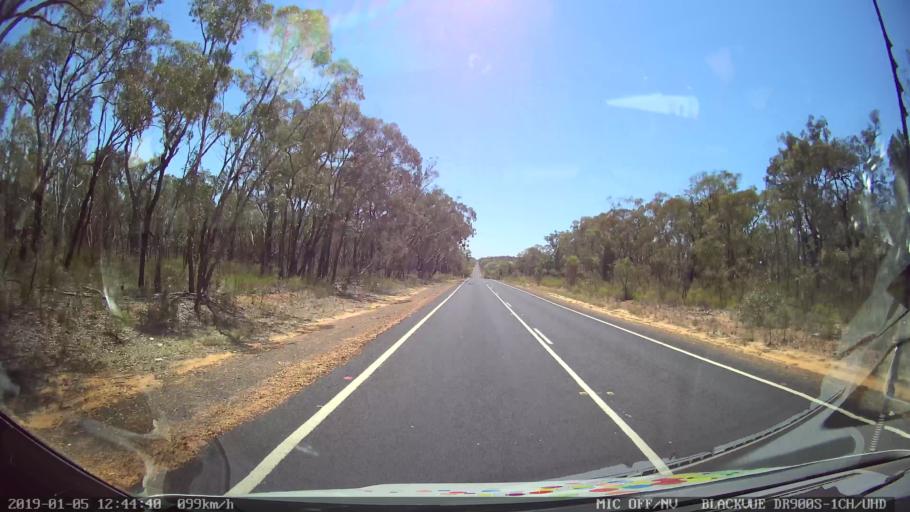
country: AU
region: New South Wales
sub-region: Warrumbungle Shire
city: Coonabarabran
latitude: -31.1355
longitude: 149.5402
